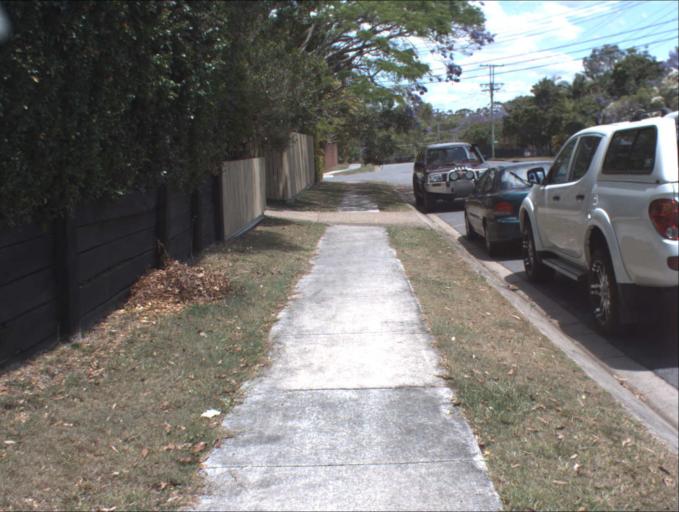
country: AU
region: Queensland
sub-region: Logan
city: Slacks Creek
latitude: -27.6419
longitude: 153.1722
